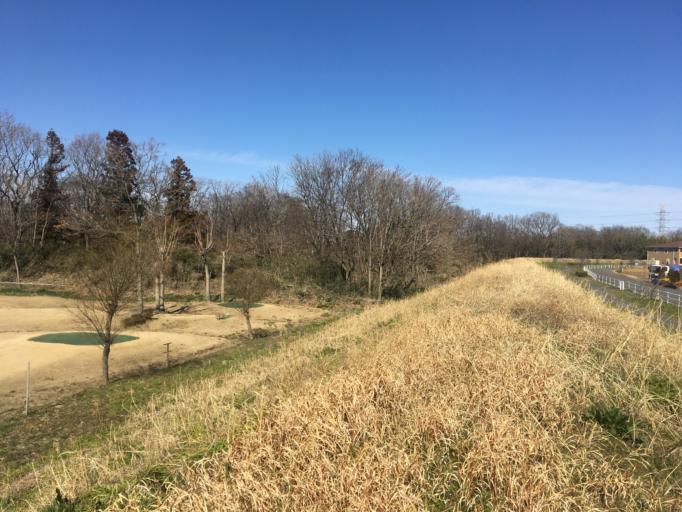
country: JP
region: Saitama
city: Sakado
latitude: 36.0073
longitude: 139.4049
